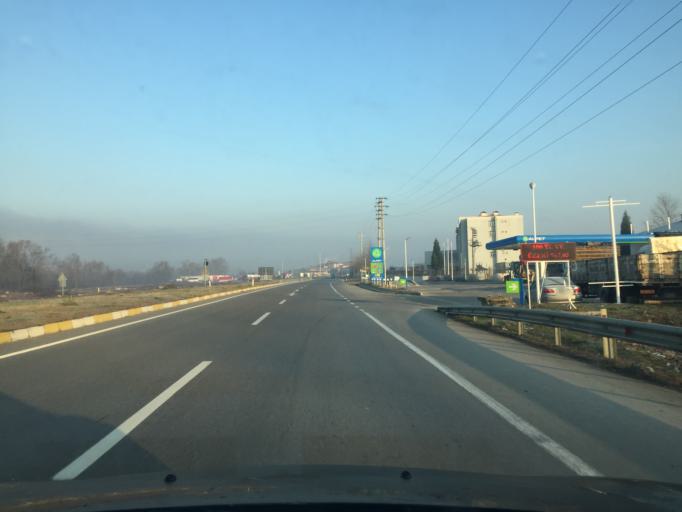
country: TR
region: Sakarya
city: Akyazi
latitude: 40.6608
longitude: 30.5966
